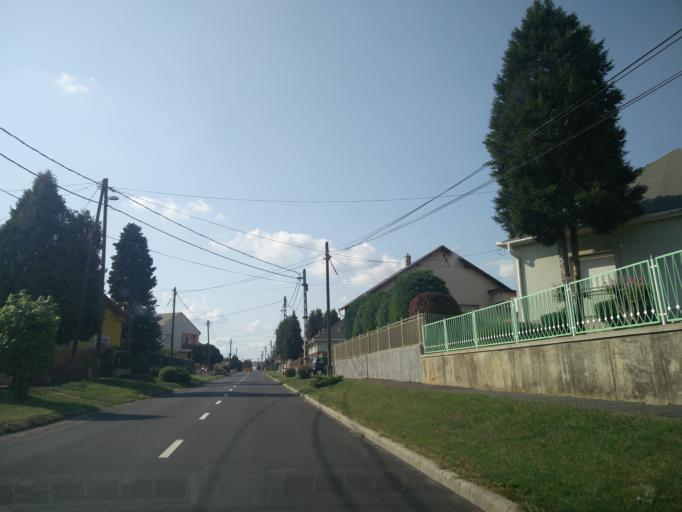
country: HU
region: Zala
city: Zalaegerszeg
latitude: 46.8689
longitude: 16.8271
